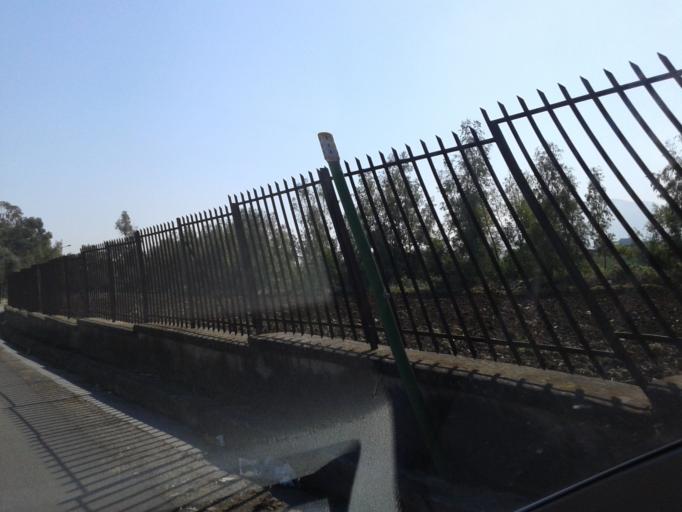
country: IT
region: Sicily
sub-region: Palermo
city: Piano dei Geli
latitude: 38.1194
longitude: 13.3029
